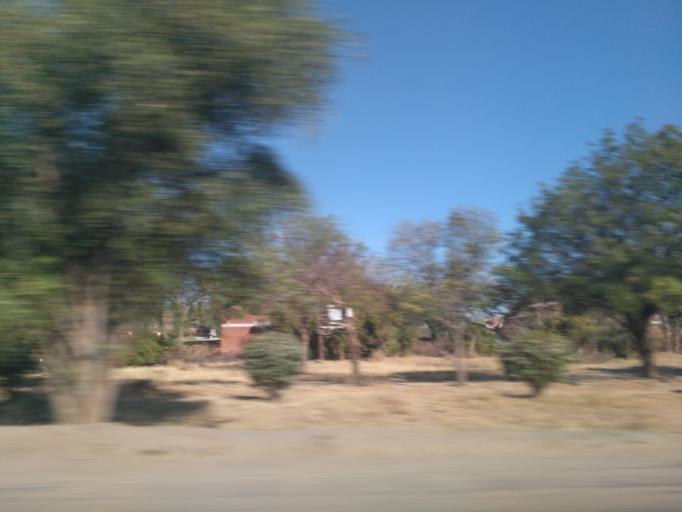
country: TZ
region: Dodoma
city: Dodoma
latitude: -6.1677
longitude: 35.7441
